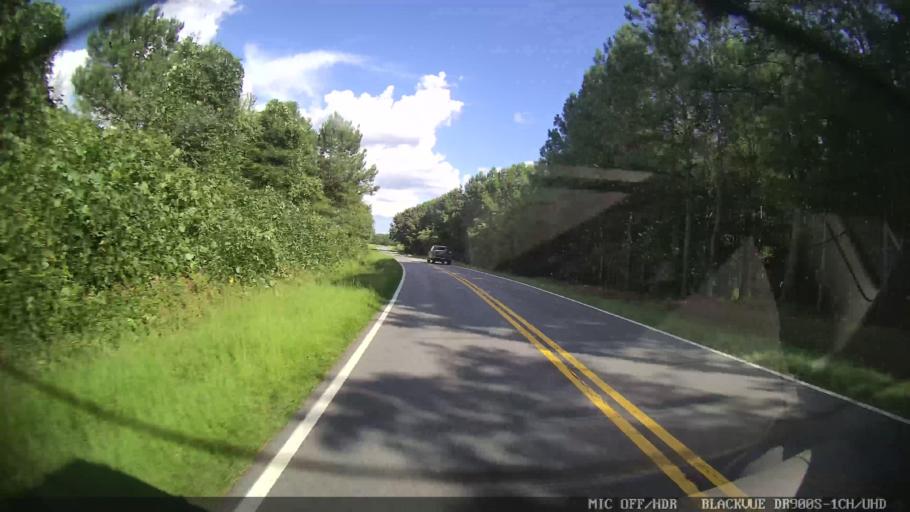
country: US
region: Georgia
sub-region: Bartow County
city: Euharlee
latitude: 34.1544
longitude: -84.9854
